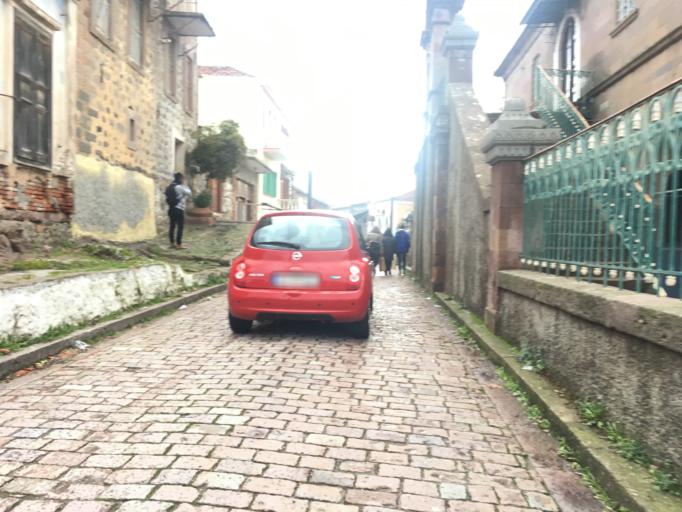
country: GR
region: North Aegean
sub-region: Nomos Lesvou
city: Agia Paraskevi
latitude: 39.2481
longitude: 26.2711
